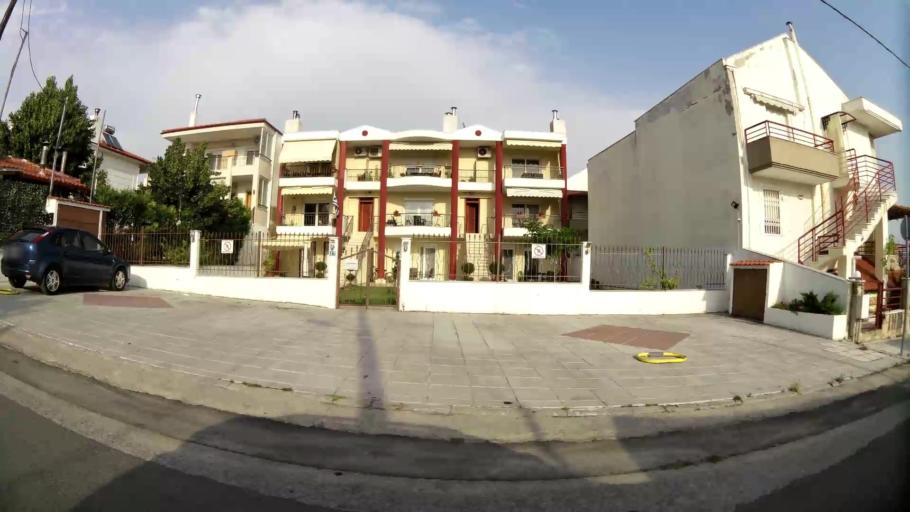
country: GR
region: Central Macedonia
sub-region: Nomos Thessalonikis
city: Oraiokastro
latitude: 40.7194
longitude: 22.9042
